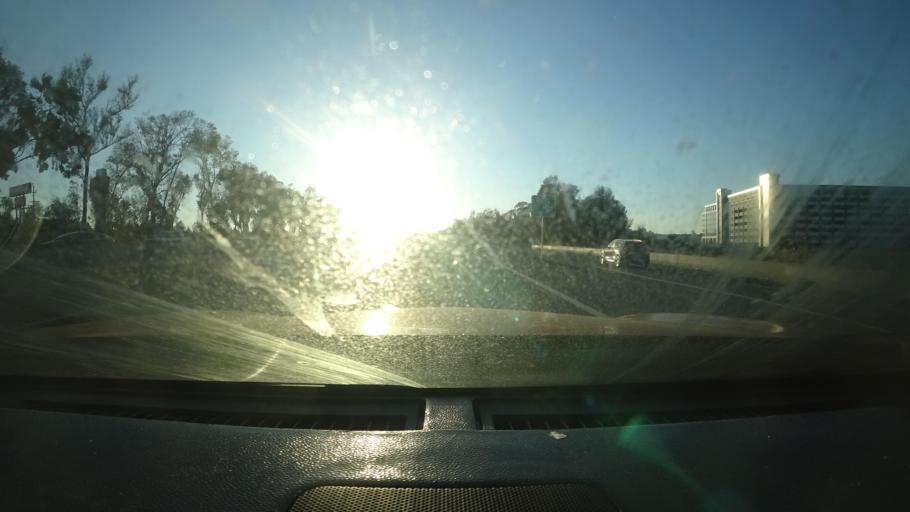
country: US
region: California
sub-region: Santa Clara County
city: San Jose
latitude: 37.3712
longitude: -121.9141
